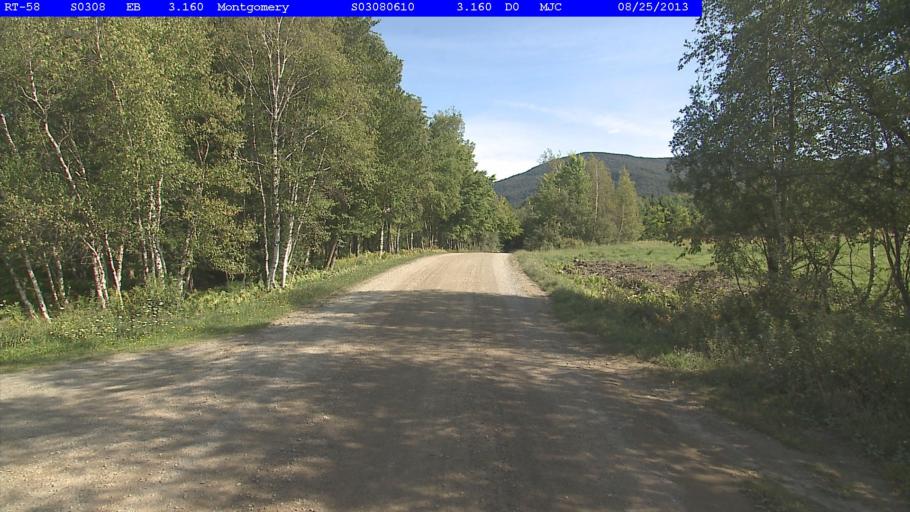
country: US
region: Vermont
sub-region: Franklin County
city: Richford
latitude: 44.8565
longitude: -72.5553
